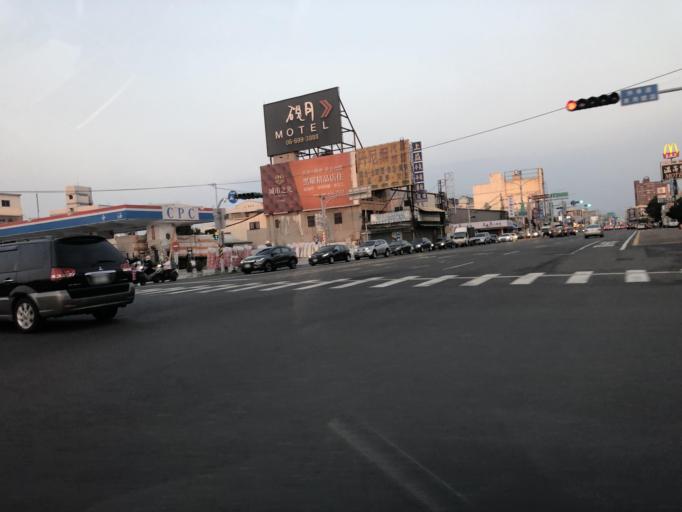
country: TW
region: Taiwan
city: Xinying
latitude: 23.3064
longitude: 120.2936
